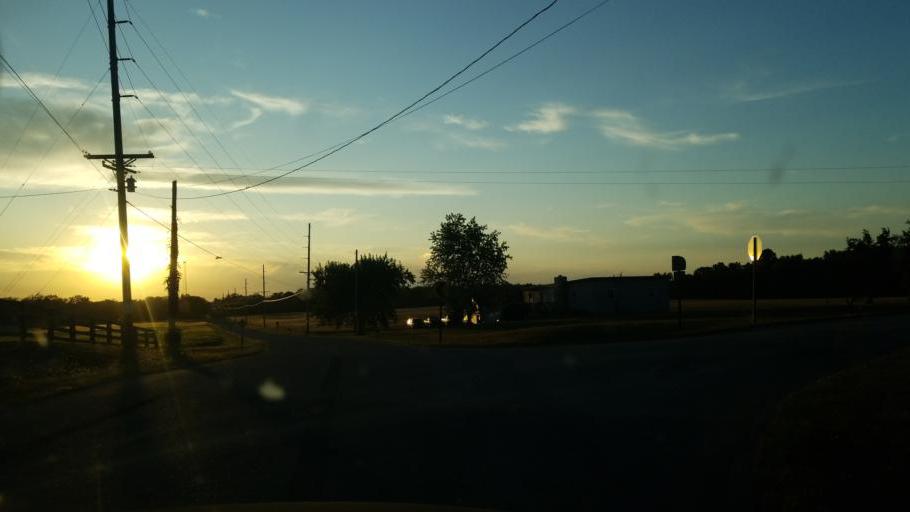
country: US
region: Ohio
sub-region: Delaware County
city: Ashley
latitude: 40.3605
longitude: -82.8844
